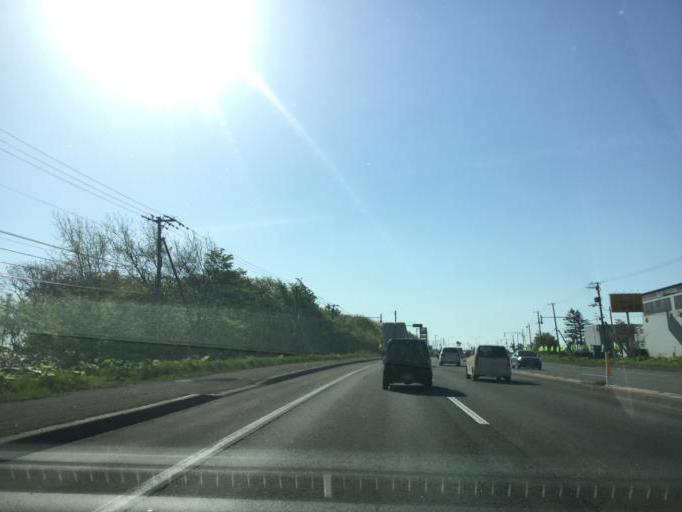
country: JP
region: Hokkaido
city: Kitahiroshima
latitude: 43.0086
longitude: 141.5193
